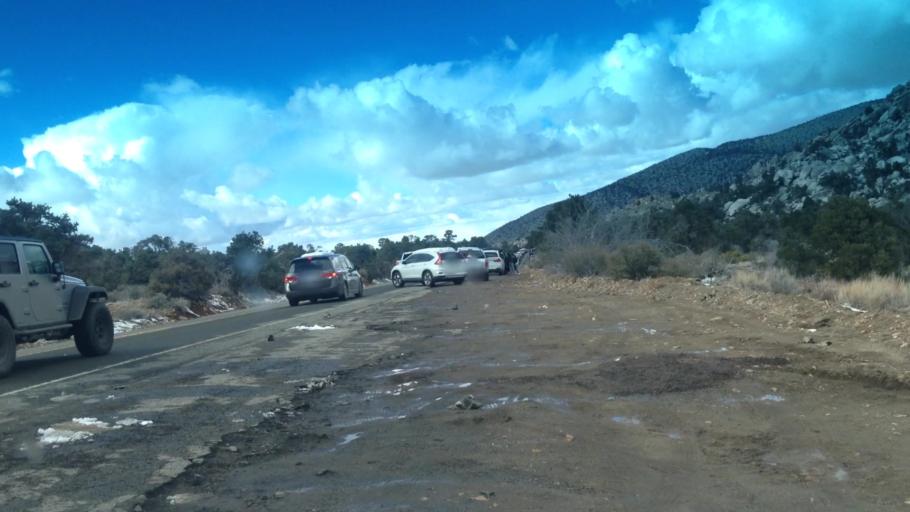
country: US
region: California
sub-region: San Bernardino County
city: Big Bear City
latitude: 34.3105
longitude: -116.8075
